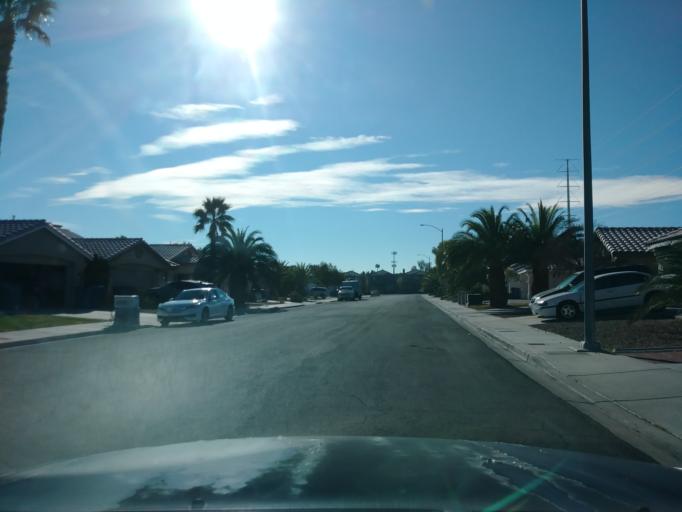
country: US
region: Nevada
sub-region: Clark County
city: Spring Valley
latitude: 36.1494
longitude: -115.2788
